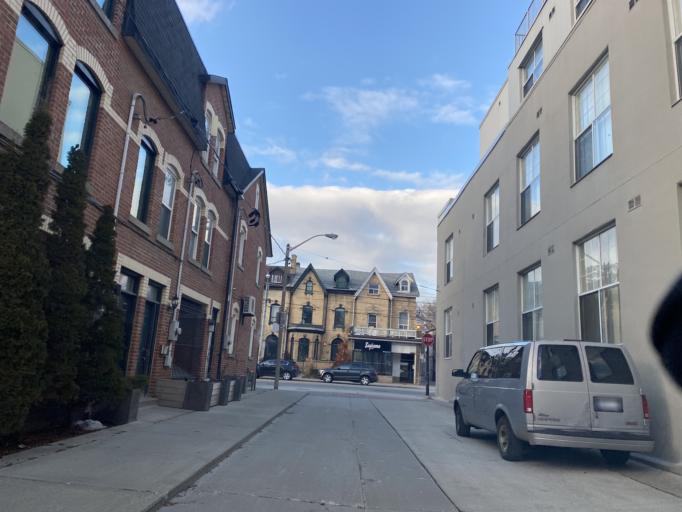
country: CA
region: Ontario
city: Toronto
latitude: 43.6590
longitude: -79.3666
